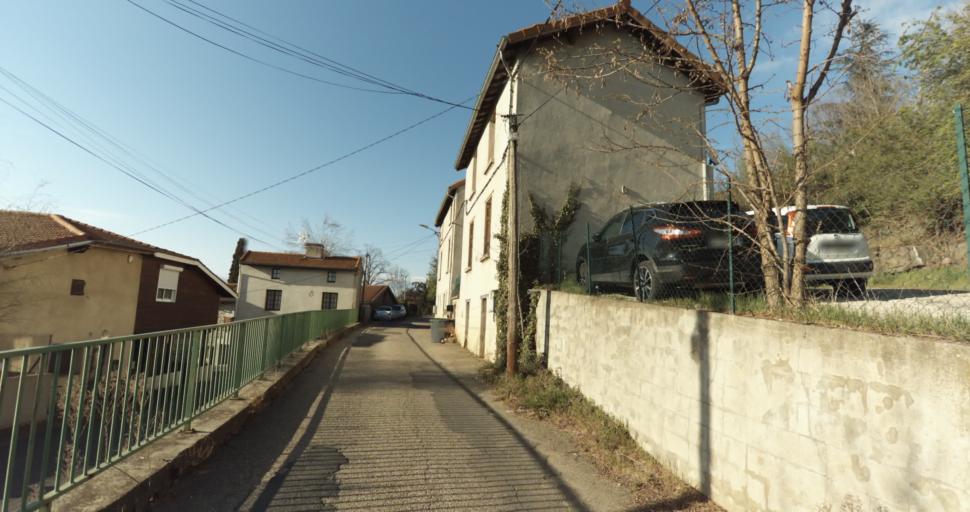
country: FR
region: Rhone-Alpes
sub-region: Departement de la Loire
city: La Talaudiere
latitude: 45.4574
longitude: 4.4260
